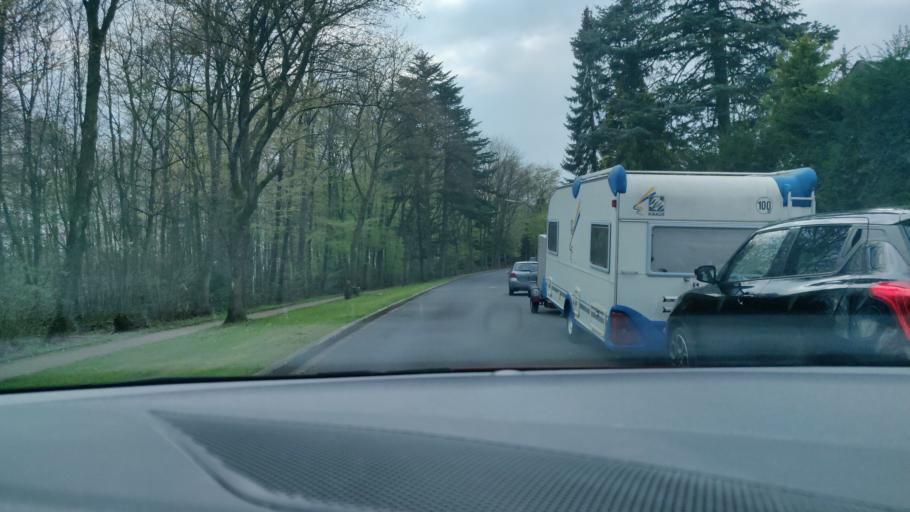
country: DE
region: North Rhine-Westphalia
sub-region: Regierungsbezirk Dusseldorf
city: Velbert
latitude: 51.3249
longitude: 7.0301
